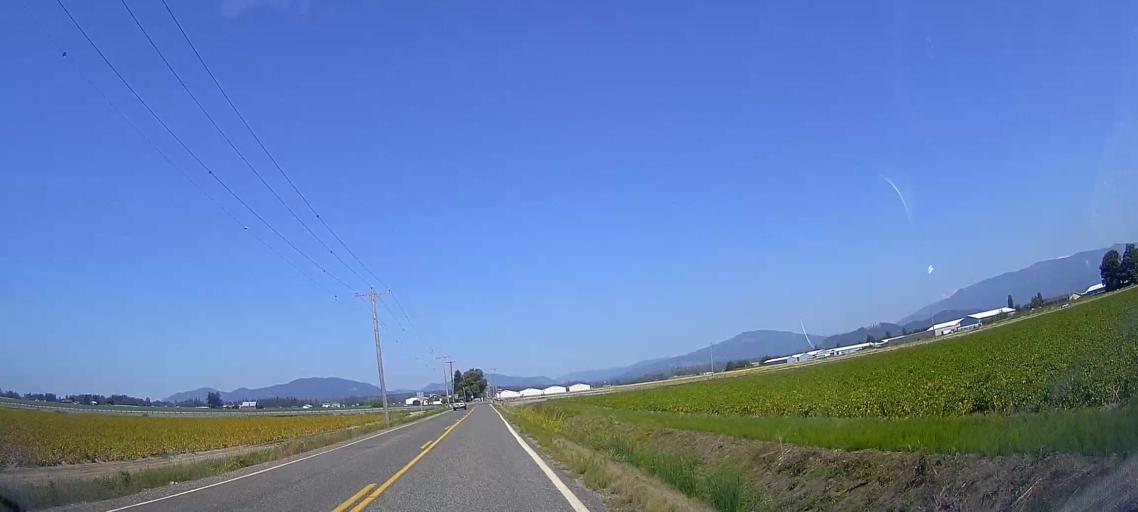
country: US
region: Washington
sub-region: Skagit County
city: Burlington
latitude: 48.4849
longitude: -122.3569
